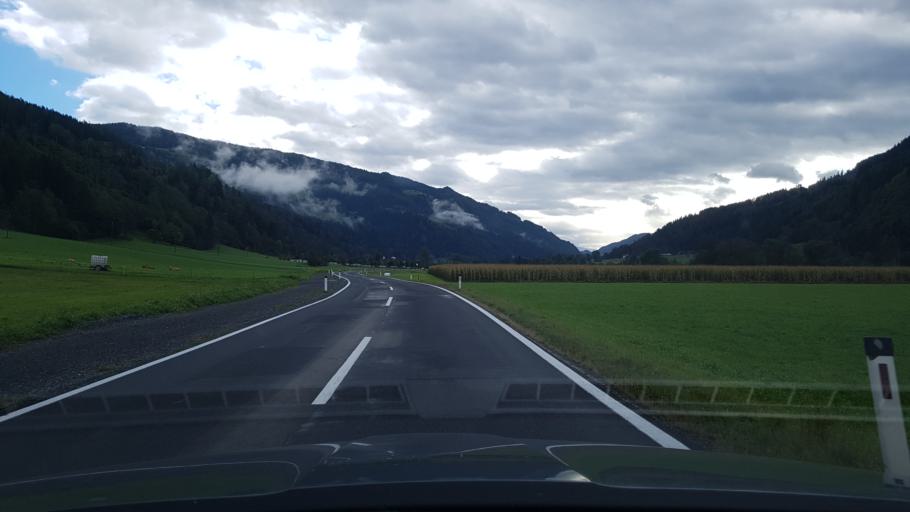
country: AT
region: Styria
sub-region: Politischer Bezirk Murau
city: Sankt Peter am Kammersberg
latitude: 47.1824
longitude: 14.2055
